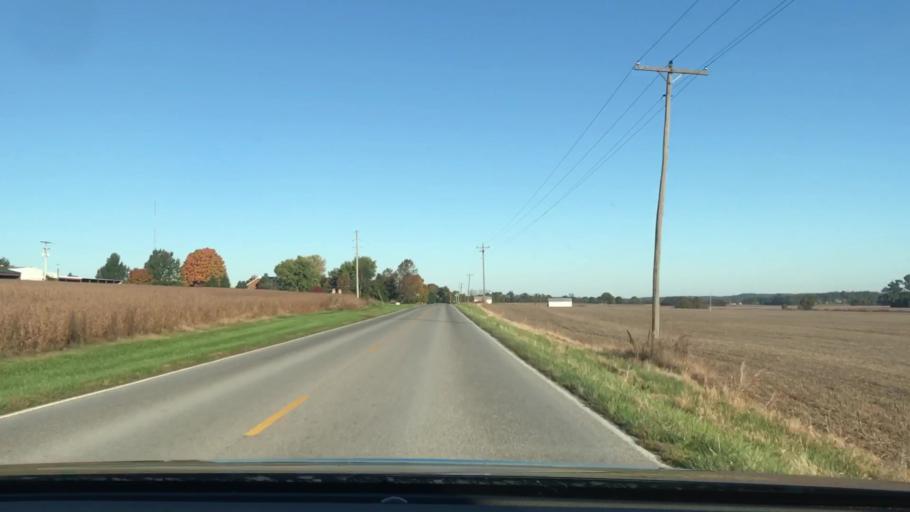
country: US
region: Kentucky
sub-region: Logan County
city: Auburn
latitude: 36.8384
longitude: -86.6907
